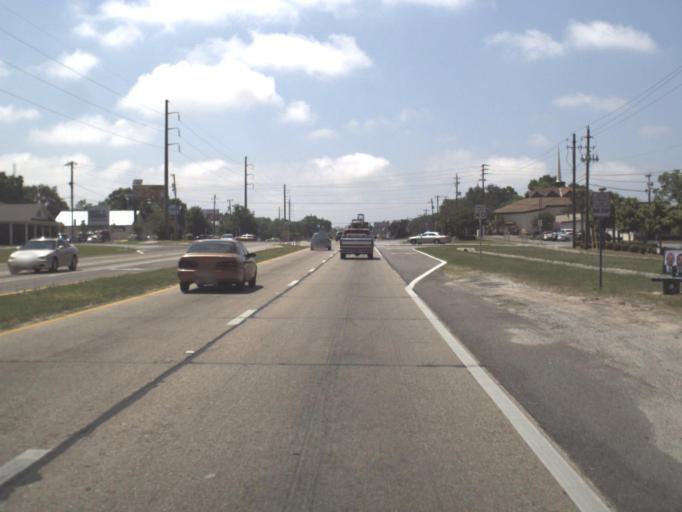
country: US
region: Florida
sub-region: Escambia County
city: Warrington
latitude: 30.3956
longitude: -87.2780
